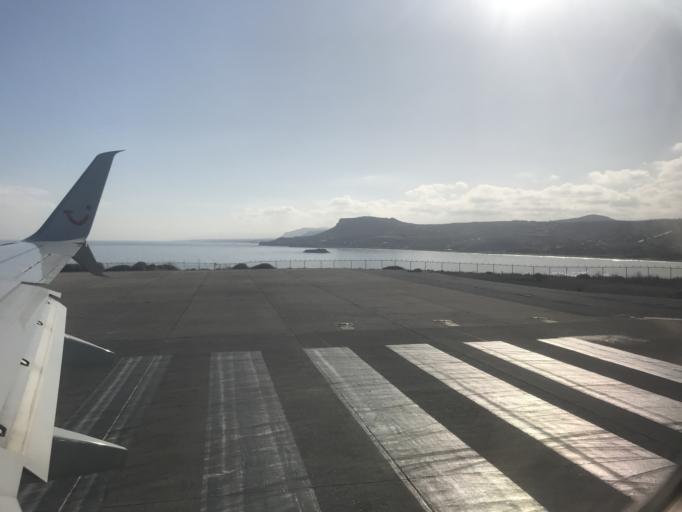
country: GR
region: Crete
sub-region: Nomos Irakleiou
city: Nea Alikarnassos
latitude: 35.3390
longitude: 25.1907
